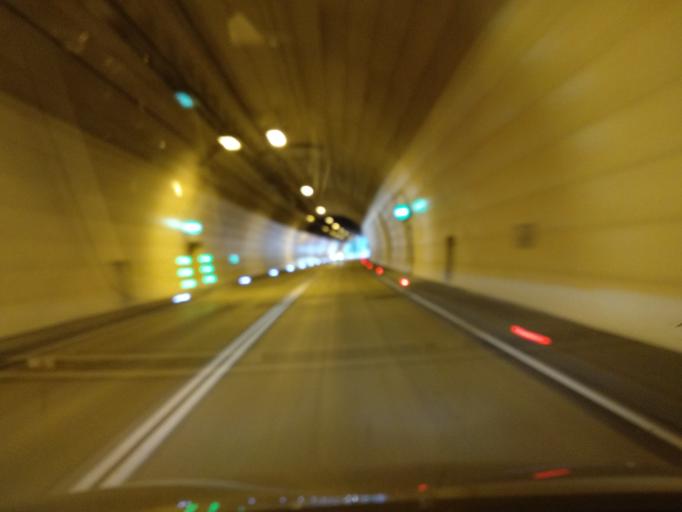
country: AT
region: Vorarlberg
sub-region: Politischer Bezirk Bludenz
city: Dalaas
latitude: 47.1261
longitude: 9.9857
